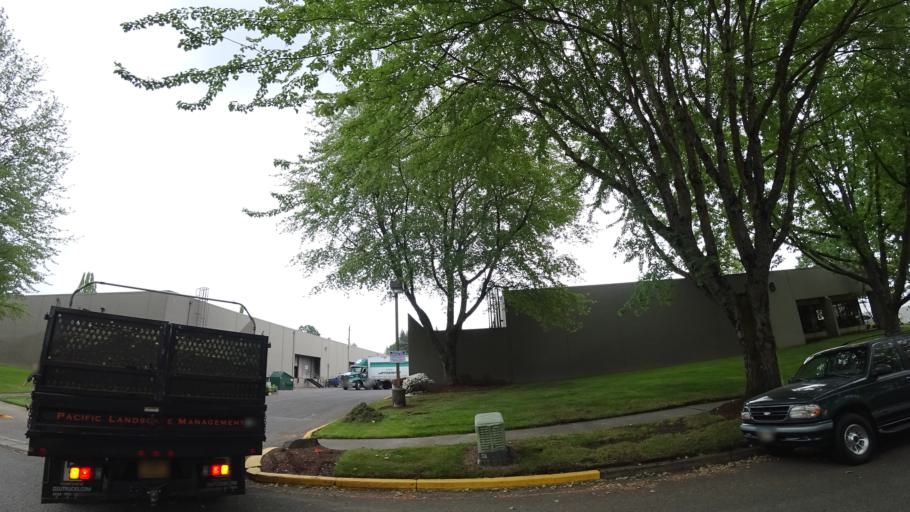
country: US
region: Oregon
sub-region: Washington County
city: Beaverton
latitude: 45.4616
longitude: -122.7887
